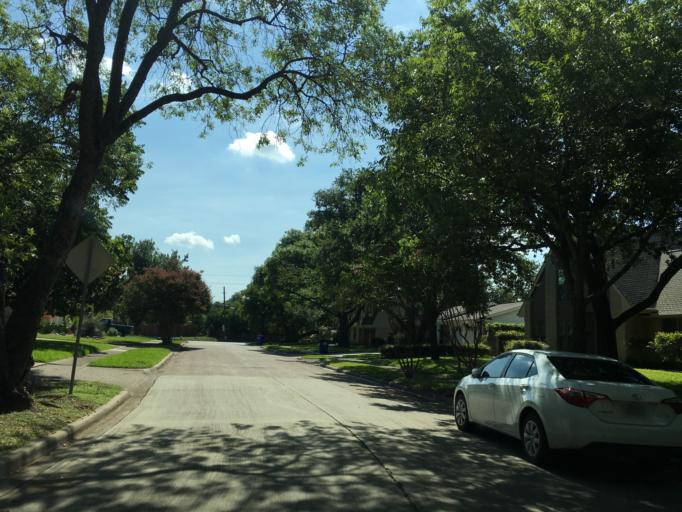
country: US
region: Texas
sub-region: Dallas County
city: Farmers Branch
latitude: 32.9170
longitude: -96.8743
